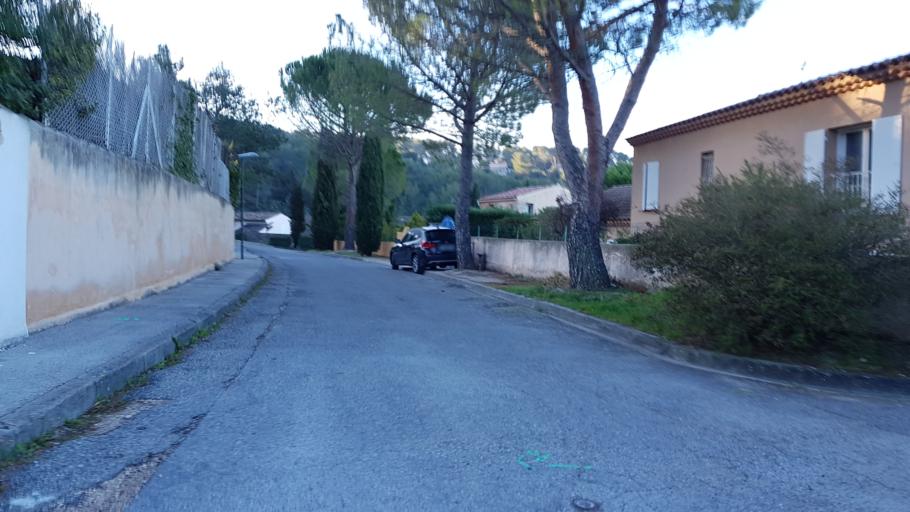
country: FR
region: Provence-Alpes-Cote d'Azur
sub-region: Departement des Bouches-du-Rhone
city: Bouc-Bel-Air
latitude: 43.4839
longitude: 5.4265
